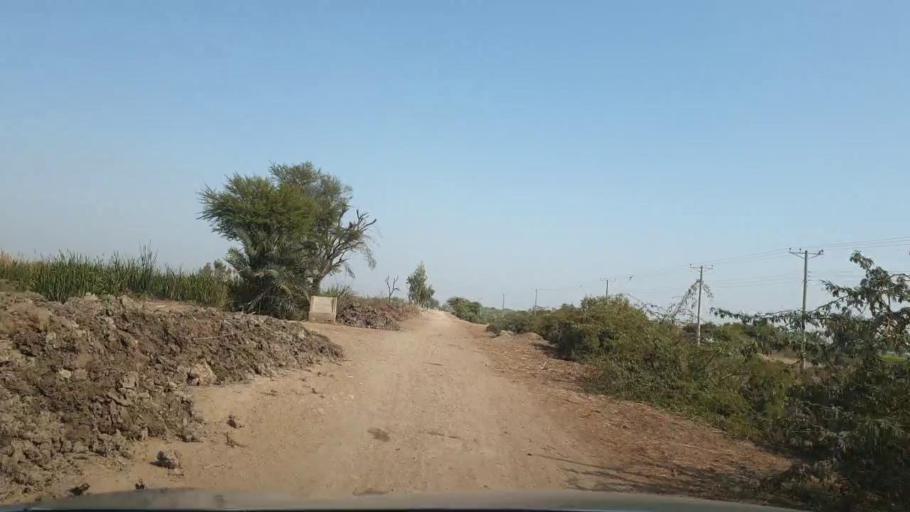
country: PK
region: Sindh
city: Berani
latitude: 25.6626
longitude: 68.8868
